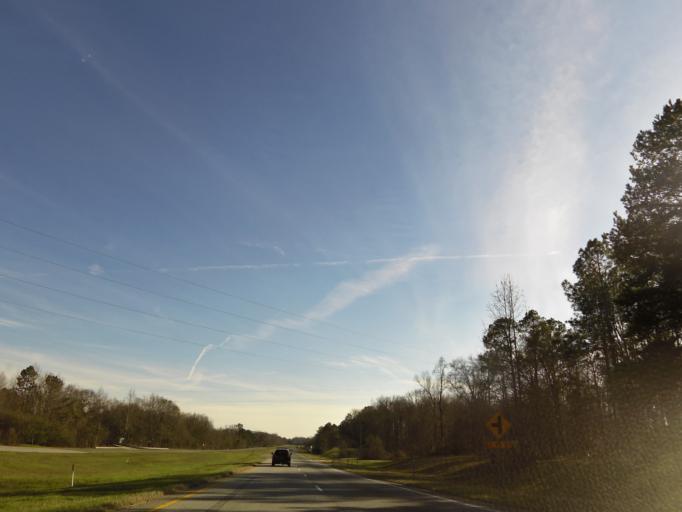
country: US
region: Georgia
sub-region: Chattahoochee County
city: Cusseta
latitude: 32.2336
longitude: -84.7132
